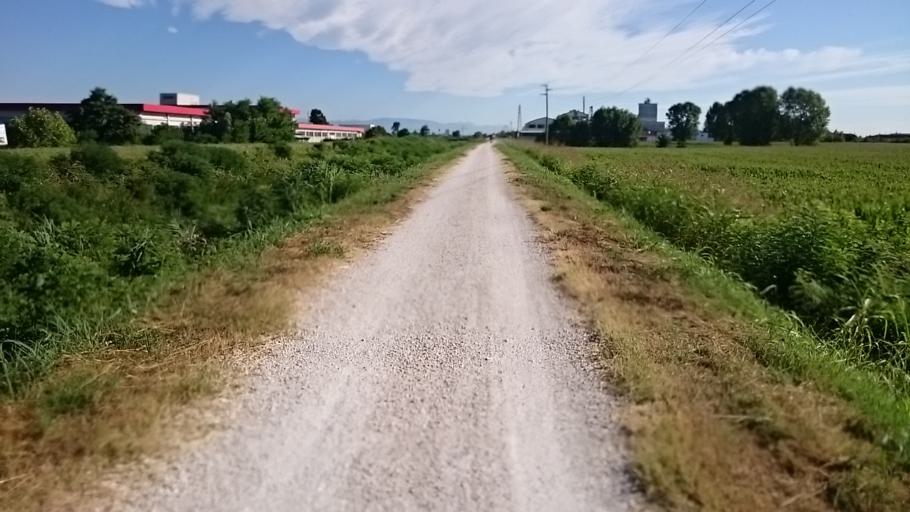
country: IT
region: Veneto
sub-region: Provincia di Padova
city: Borgoricco-San Michele delle Badesse-Sant'Eufemia
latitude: 45.5345
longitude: 11.9244
